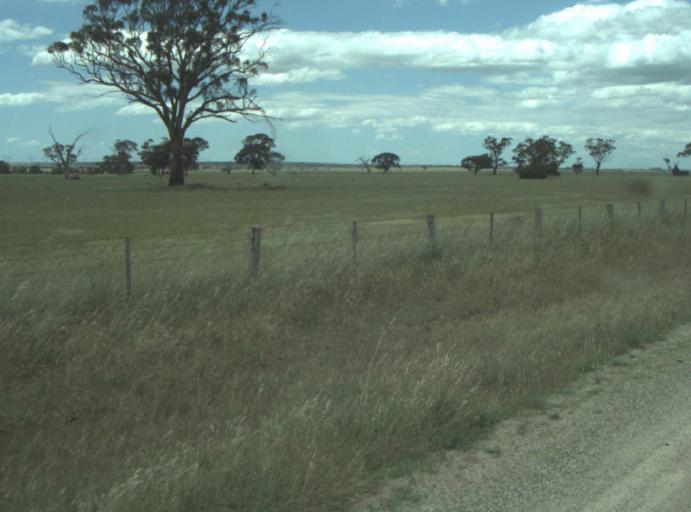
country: AU
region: Victoria
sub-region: Wyndham
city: Little River
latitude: -37.8779
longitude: 144.4187
